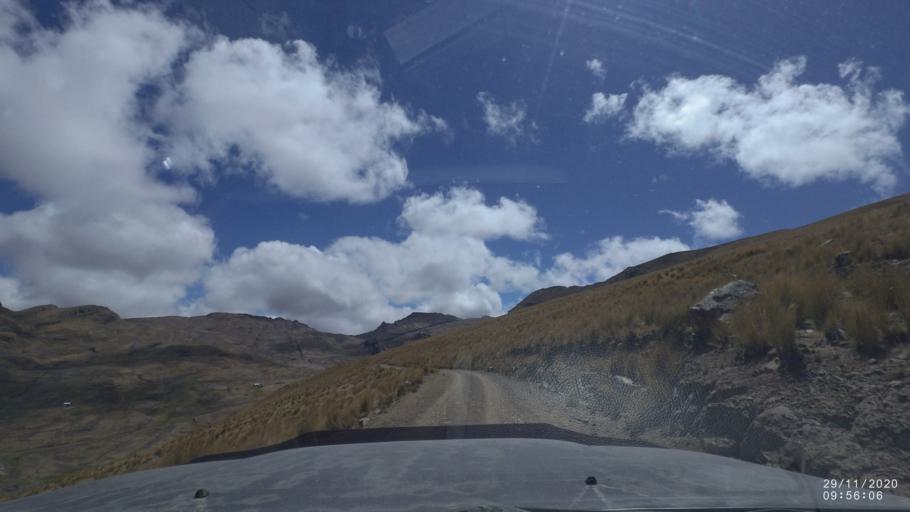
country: BO
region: Cochabamba
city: Cochabamba
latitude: -17.2727
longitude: -66.1757
